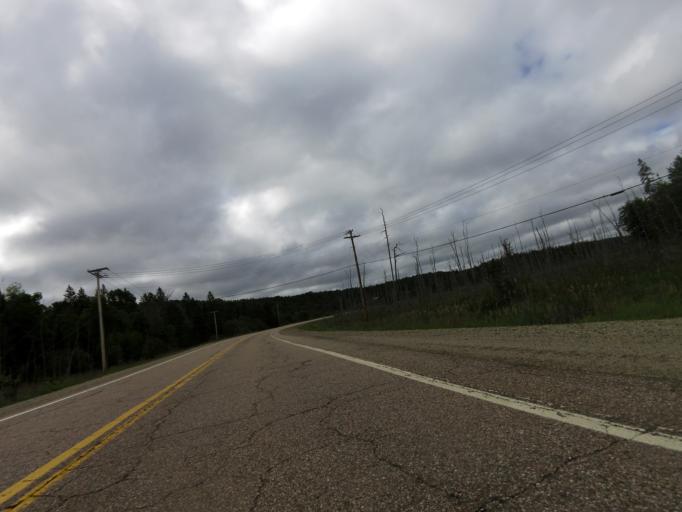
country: CA
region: Quebec
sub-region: Outaouais
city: Shawville
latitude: 45.8143
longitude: -76.4596
